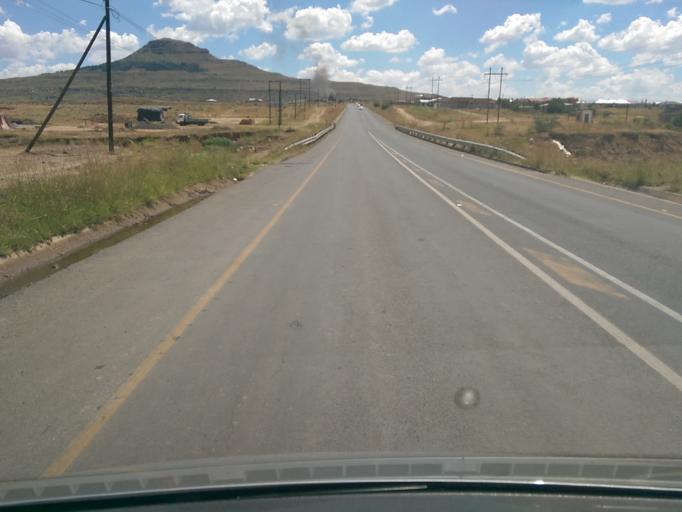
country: LS
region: Maseru
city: Maseru
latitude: -29.3764
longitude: 27.4844
